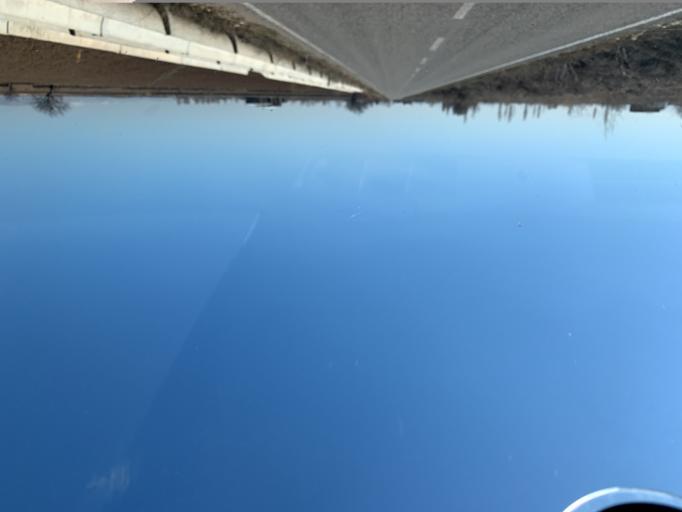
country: TR
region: Konya
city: Cumra
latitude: 37.6175
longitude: 32.7992
